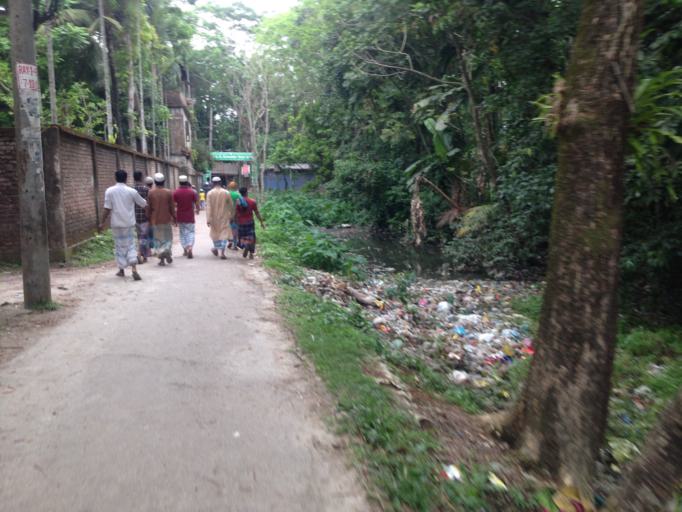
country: BD
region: Chittagong
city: Raipur
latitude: 23.0352
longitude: 90.7715
